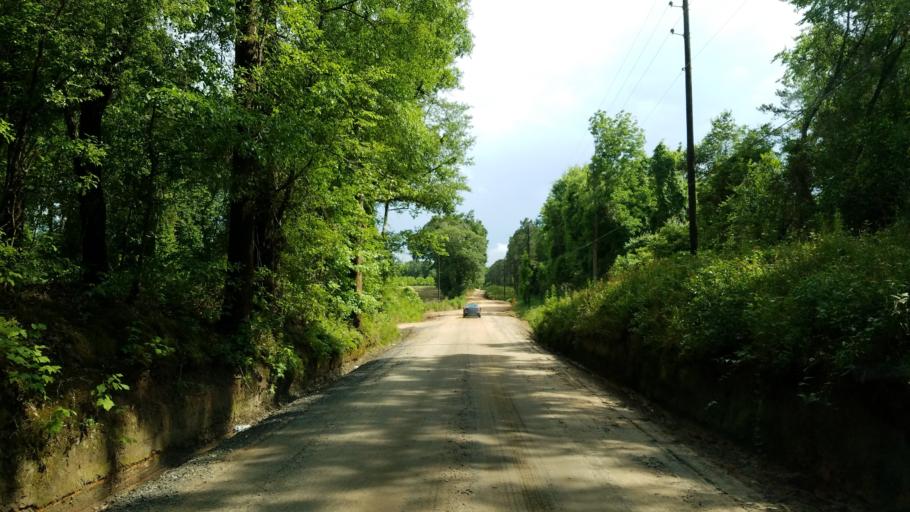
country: US
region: Georgia
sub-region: Houston County
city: Perry
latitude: 32.4447
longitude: -83.7891
